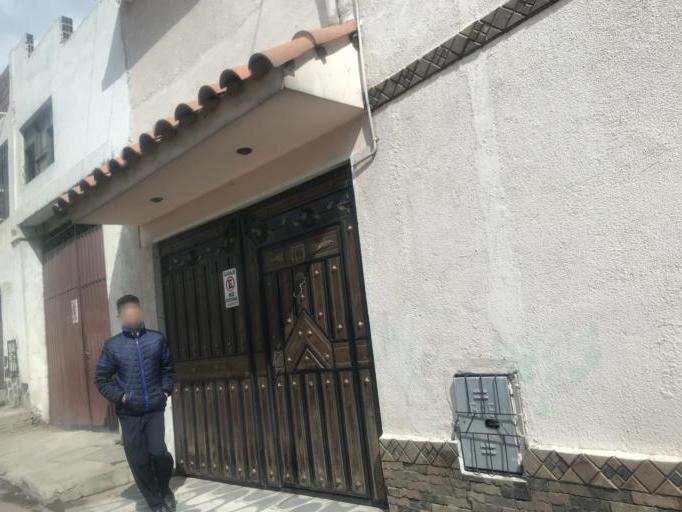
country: BO
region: Potosi
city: Potosi
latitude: -19.5939
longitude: -65.7512
